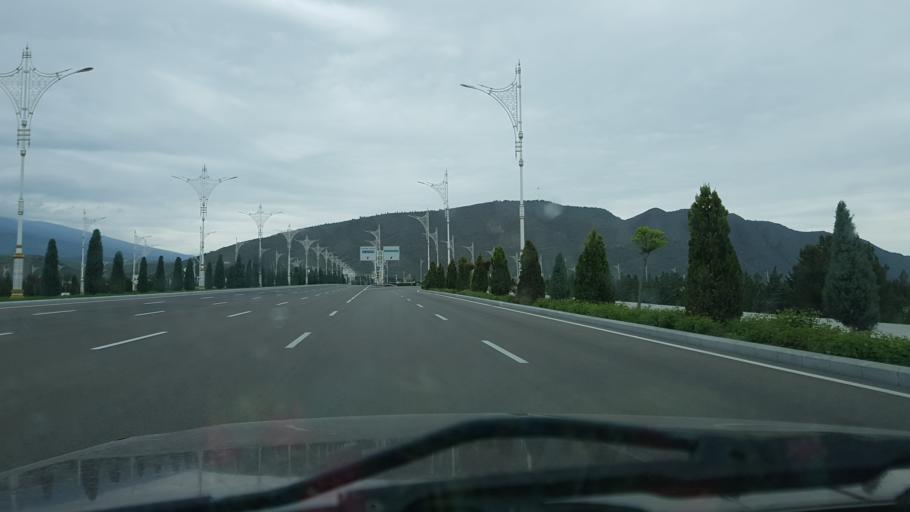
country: TM
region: Ahal
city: Ashgabat
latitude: 37.8964
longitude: 58.2583
